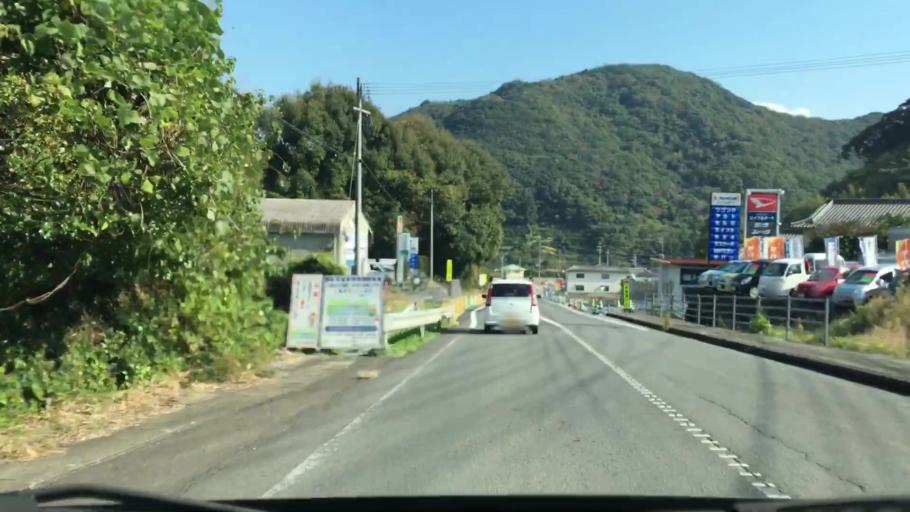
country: JP
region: Nagasaki
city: Togitsu
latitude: 32.8601
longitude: 129.8035
